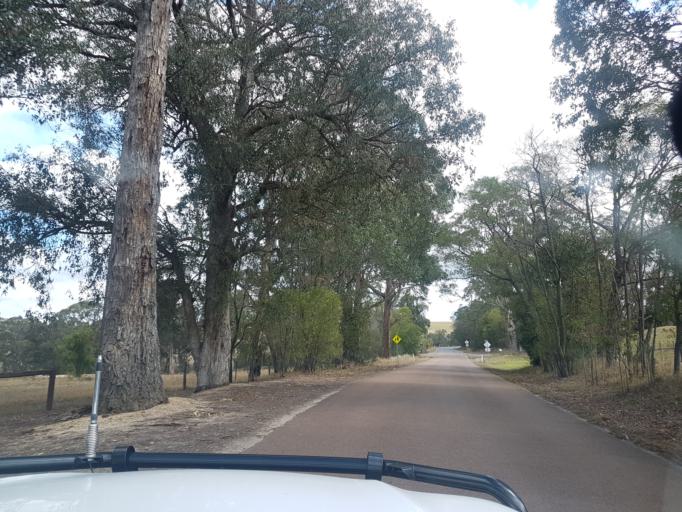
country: AU
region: Victoria
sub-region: East Gippsland
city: Bairnsdale
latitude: -37.7886
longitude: 147.5863
